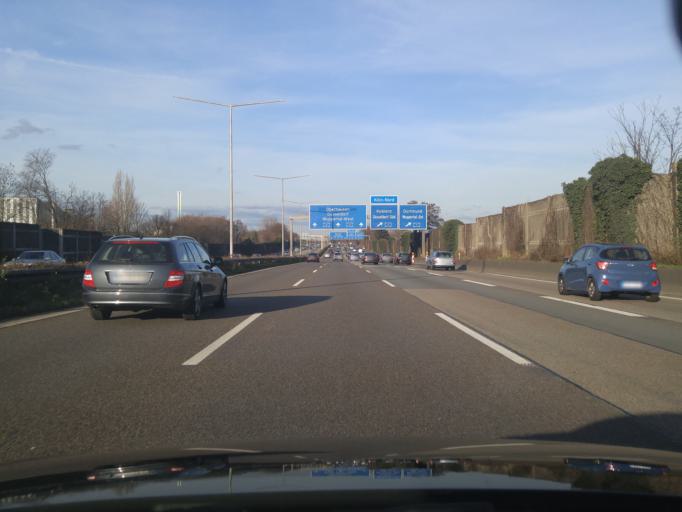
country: DE
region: North Rhine-Westphalia
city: Opladen
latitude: 51.0329
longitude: 7.0098
